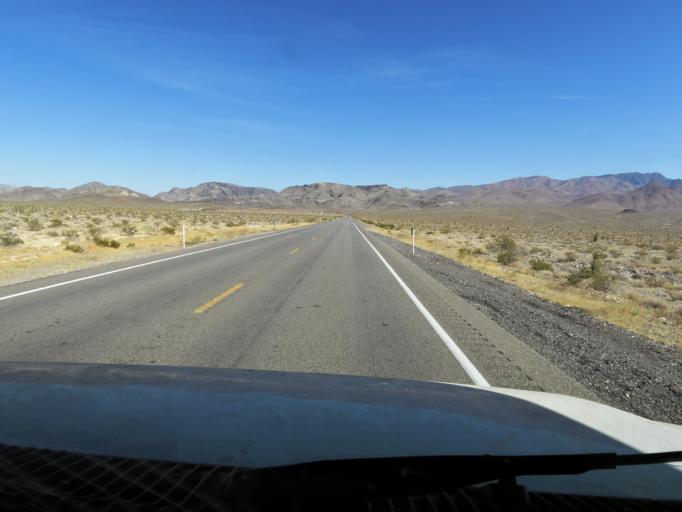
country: US
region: Nevada
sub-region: Nye County
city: Pahrump
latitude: 36.5635
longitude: -116.1140
